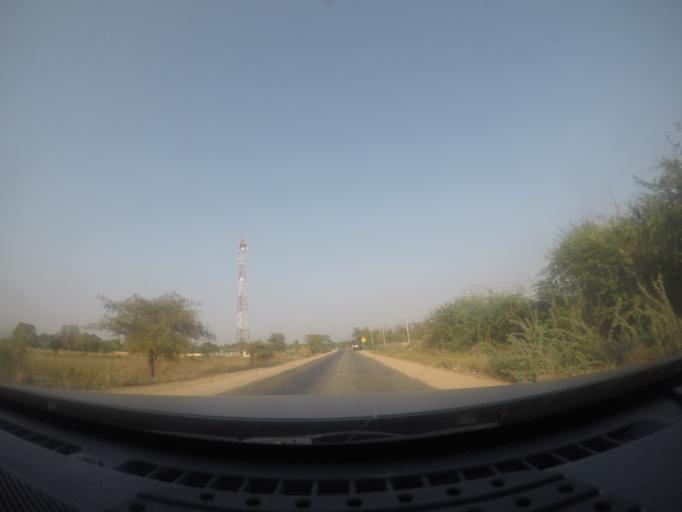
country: MM
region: Mandalay
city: Yamethin
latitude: 20.6717
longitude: 96.1364
